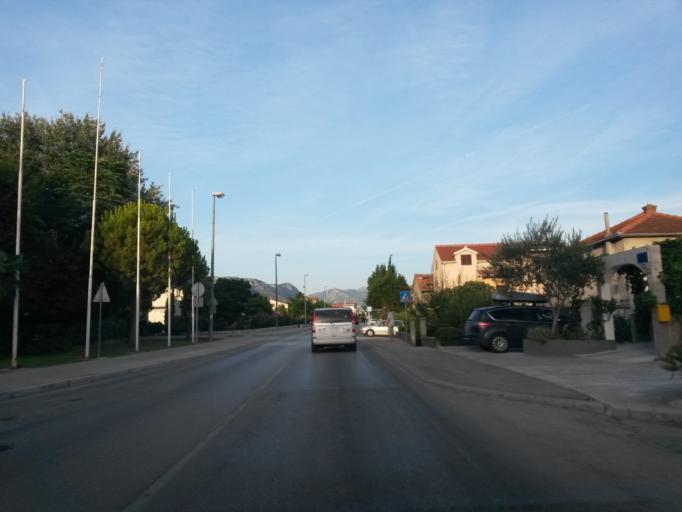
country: HR
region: Splitsko-Dalmatinska
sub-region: Grad Split
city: Split
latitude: 43.5536
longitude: 16.3644
